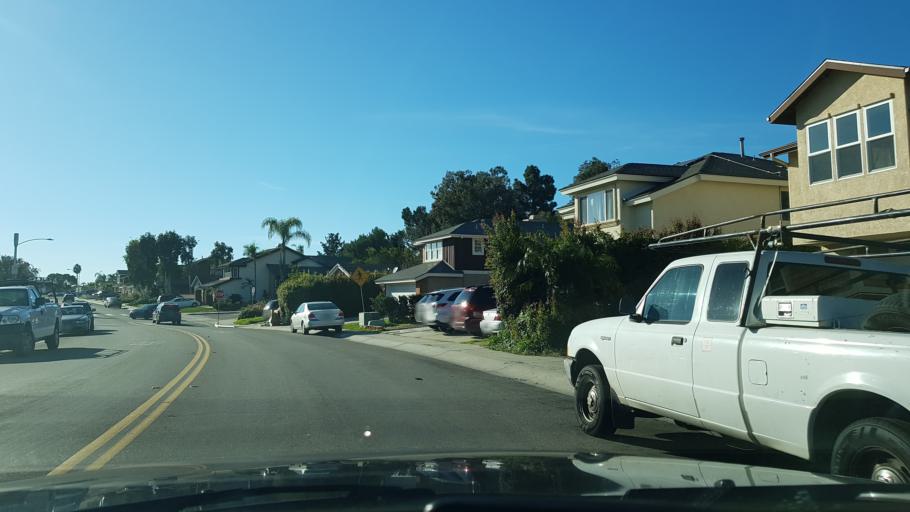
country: US
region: California
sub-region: San Diego County
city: Fairbanks Ranch
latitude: 32.9074
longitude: -117.1568
